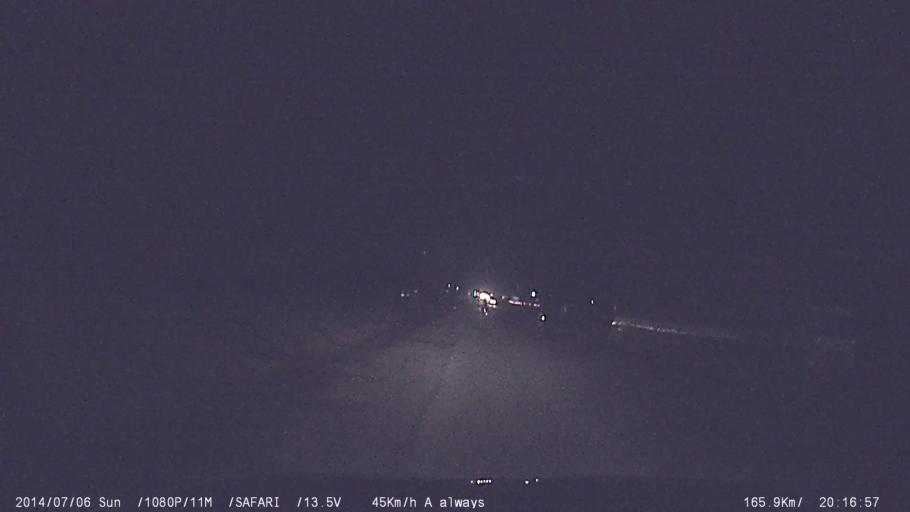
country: IN
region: Kerala
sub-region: Palakkad district
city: Palakkad
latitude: 10.7726
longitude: 76.6941
